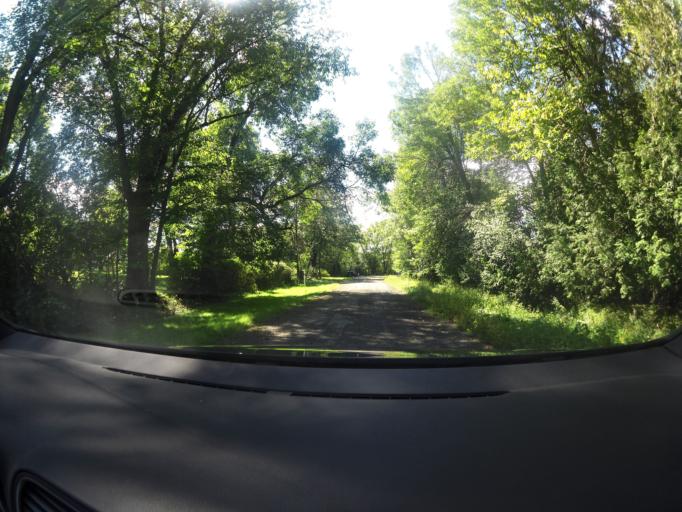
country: CA
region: Ontario
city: Carleton Place
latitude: 45.1587
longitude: -76.1067
